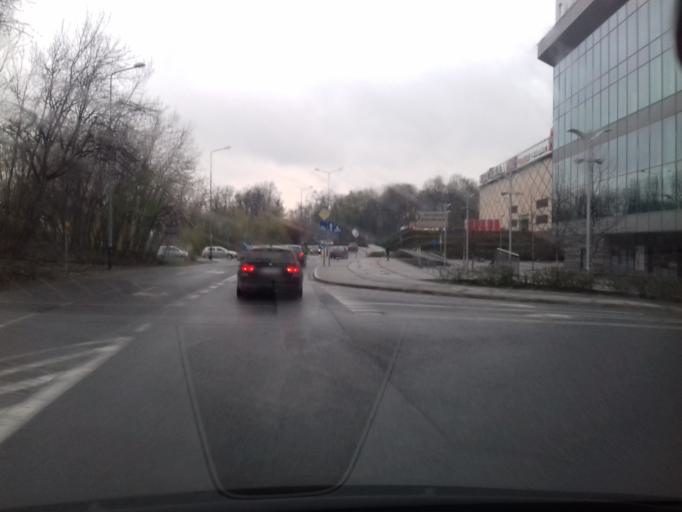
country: PL
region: Lesser Poland Voivodeship
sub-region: Krakow
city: Krakow
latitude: 50.0272
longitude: 19.9484
